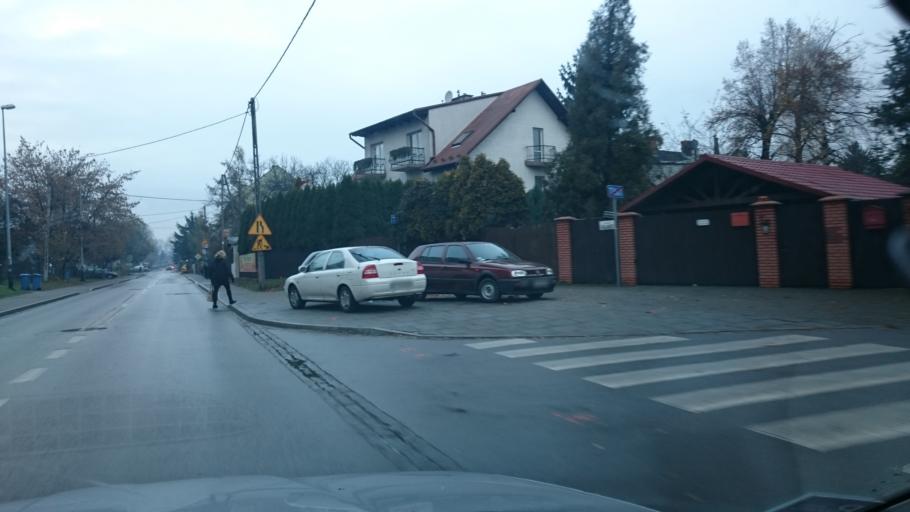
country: PL
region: Lesser Poland Voivodeship
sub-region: Krakow
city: Krakow
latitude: 50.0234
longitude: 19.9975
